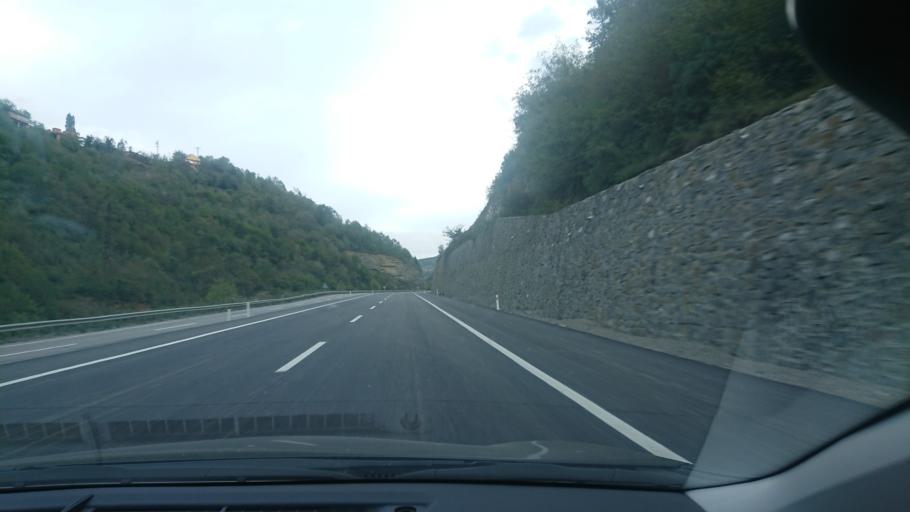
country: TR
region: Zonguldak
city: Beycuma
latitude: 41.3901
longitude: 31.9360
